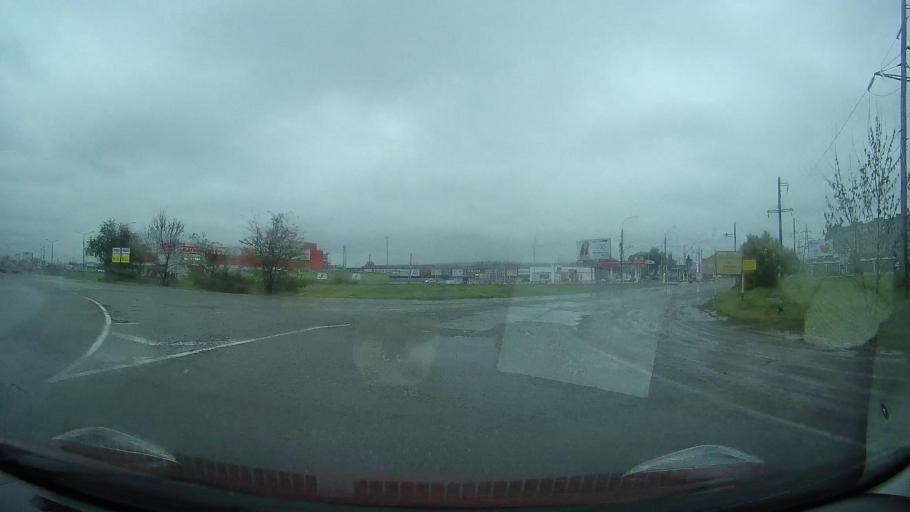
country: RU
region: Stavropol'skiy
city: Nevinnomyssk
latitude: 44.6418
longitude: 41.9595
